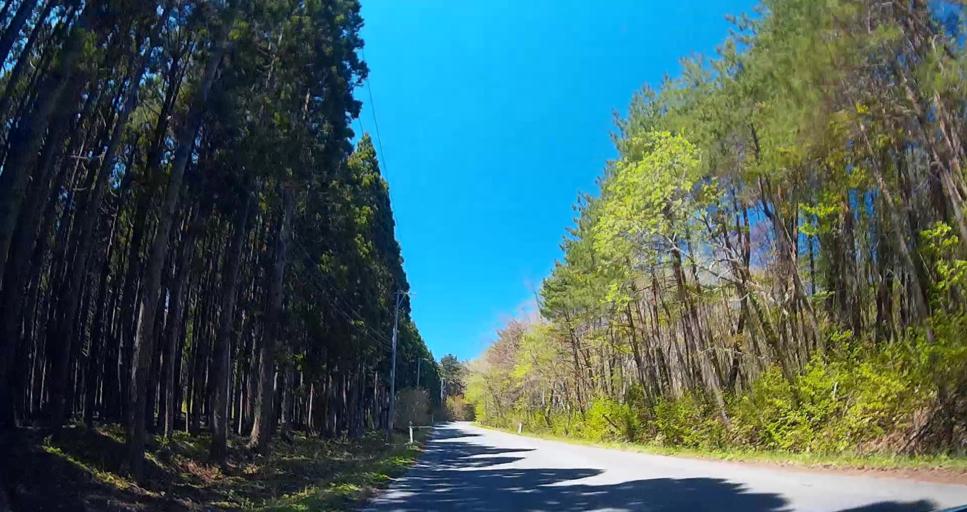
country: JP
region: Aomori
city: Mutsu
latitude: 41.2493
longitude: 141.3918
